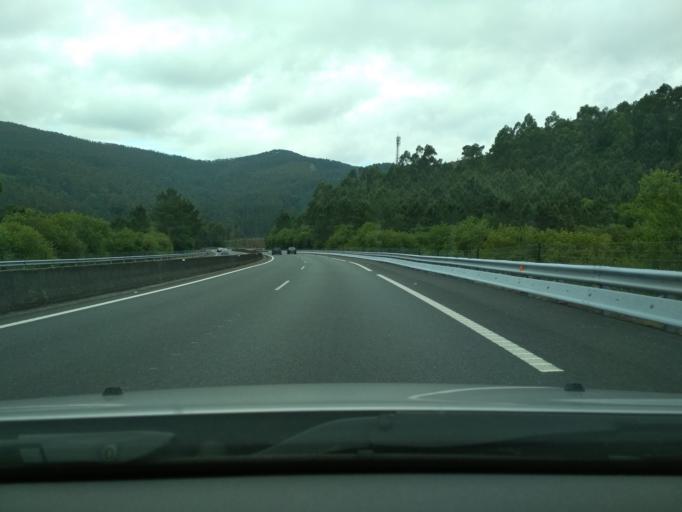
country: ES
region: Galicia
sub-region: Provincia da Coruna
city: Padron
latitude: 42.8030
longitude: -8.6227
